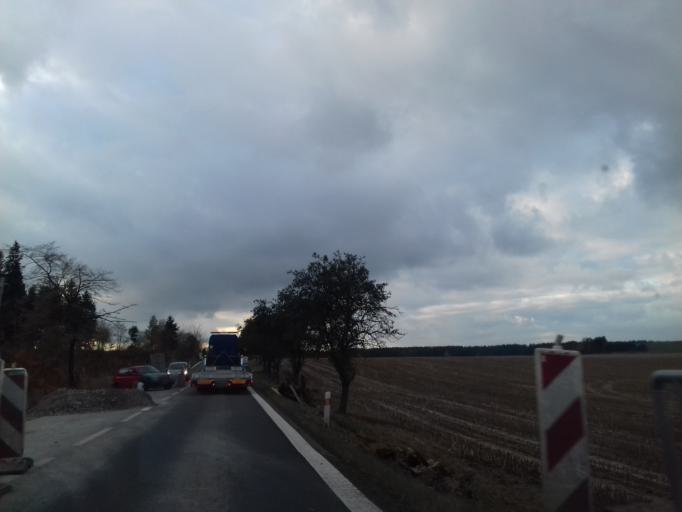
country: CZ
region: Pardubicky
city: Pomezi
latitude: 49.7322
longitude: 16.3386
